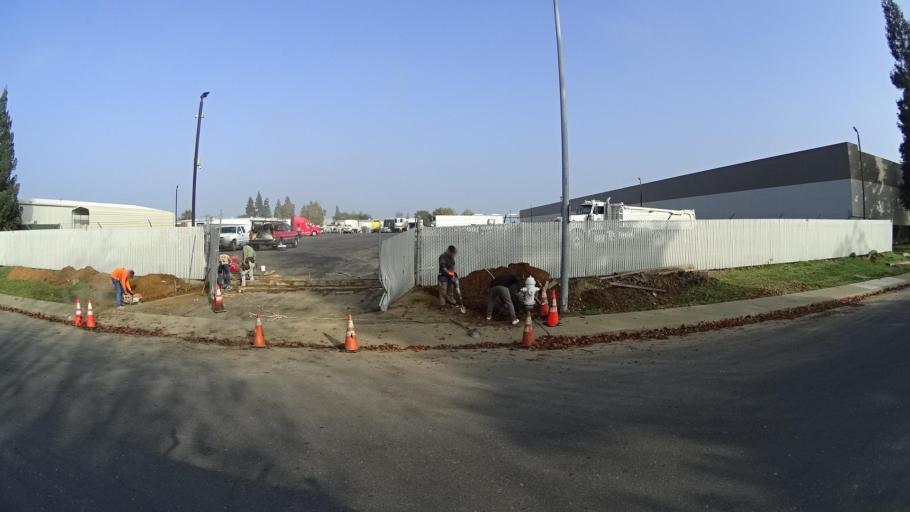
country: US
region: California
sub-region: Sacramento County
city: Elk Grove
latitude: 38.3980
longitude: -121.3557
